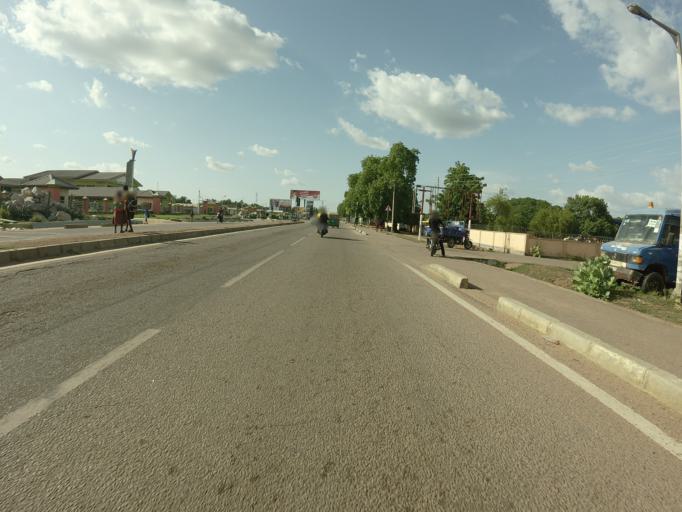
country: GH
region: Upper East
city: Bolgatanga
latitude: 10.7764
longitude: -0.8550
